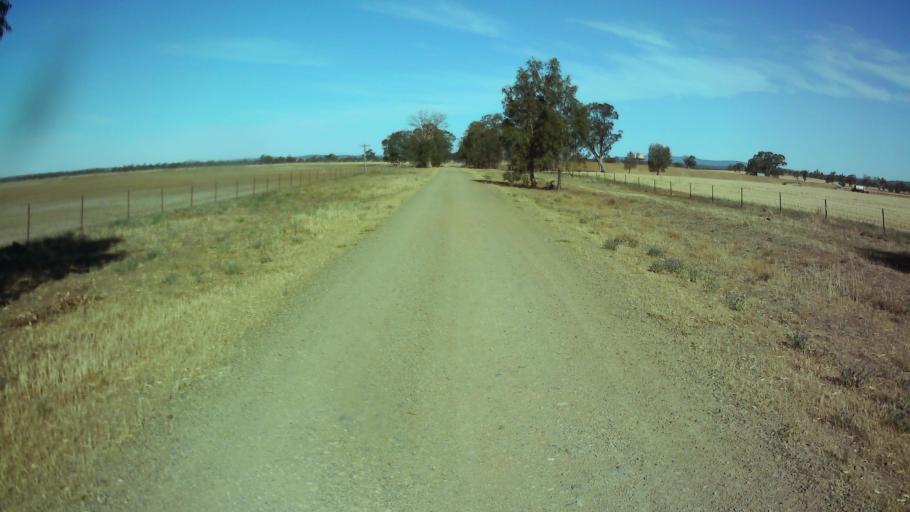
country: AU
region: New South Wales
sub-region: Weddin
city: Grenfell
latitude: -33.6579
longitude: 148.0975
